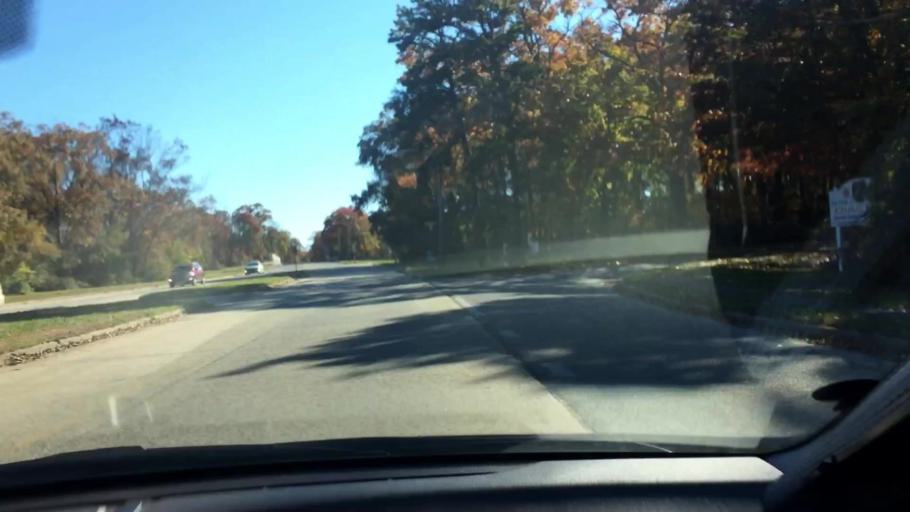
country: US
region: New York
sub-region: Suffolk County
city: West Babylon
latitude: 40.7347
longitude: -73.3467
